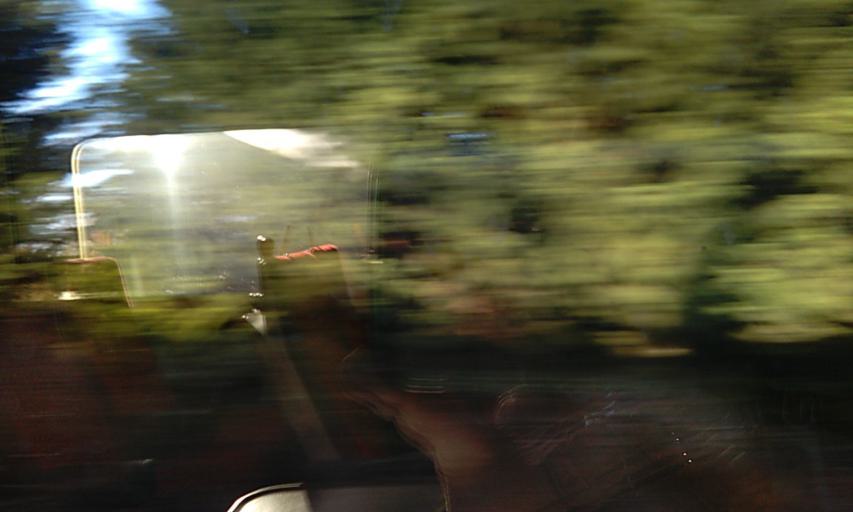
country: GB
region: England
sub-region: Derbyshire
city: Long Eaton
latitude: 52.9060
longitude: -1.2318
